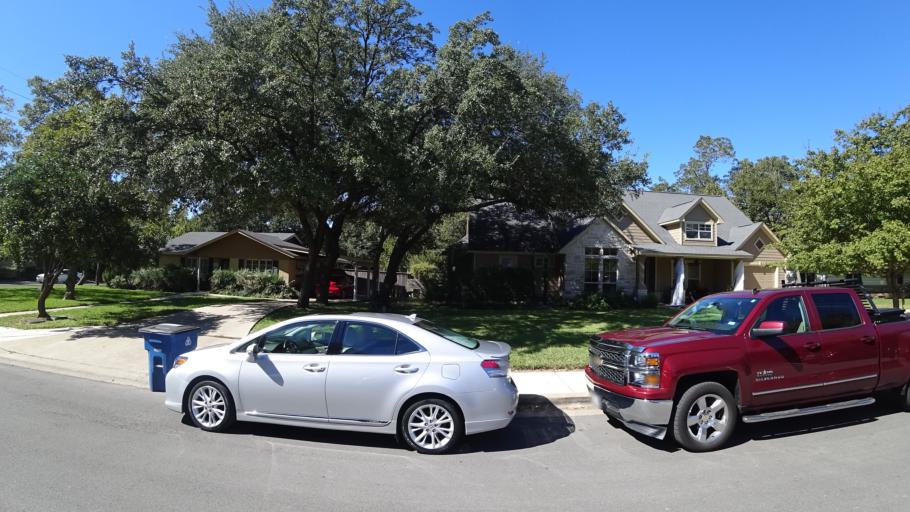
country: US
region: Texas
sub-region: Travis County
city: Austin
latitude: 30.3354
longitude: -97.7418
